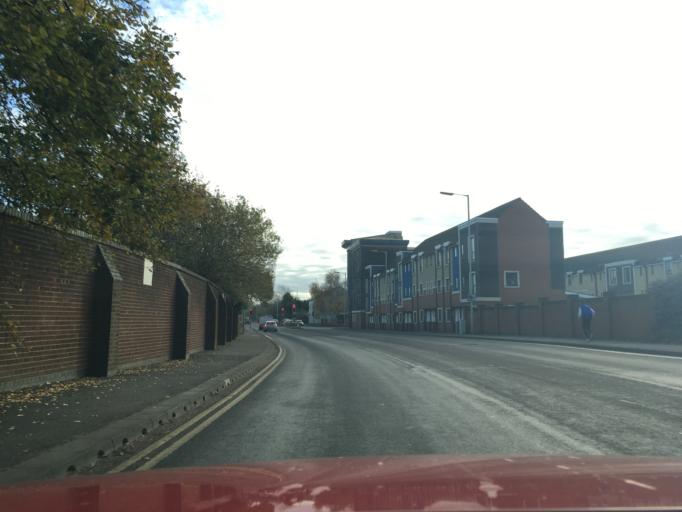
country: GB
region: England
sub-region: Staffordshire
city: Burton upon Trent
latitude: 52.8003
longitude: -1.6419
